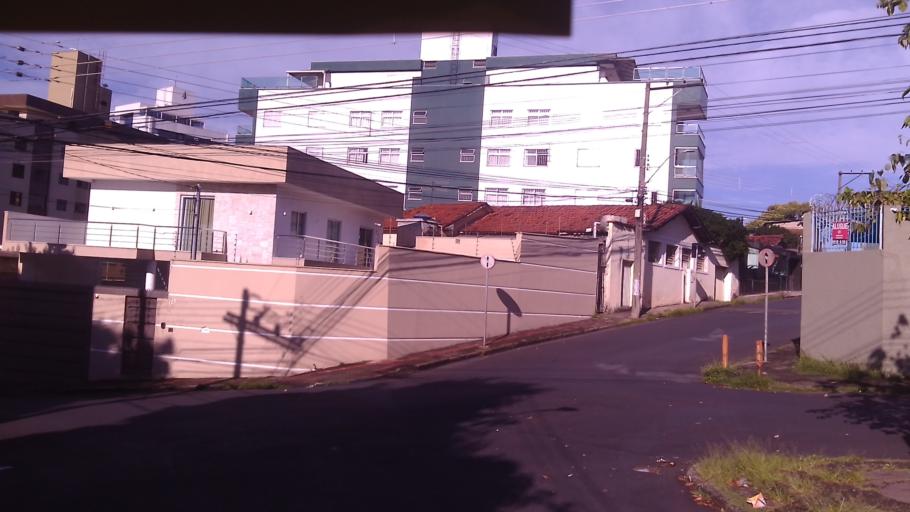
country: BR
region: Minas Gerais
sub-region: Belo Horizonte
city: Belo Horizonte
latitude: -19.9159
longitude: -43.9723
